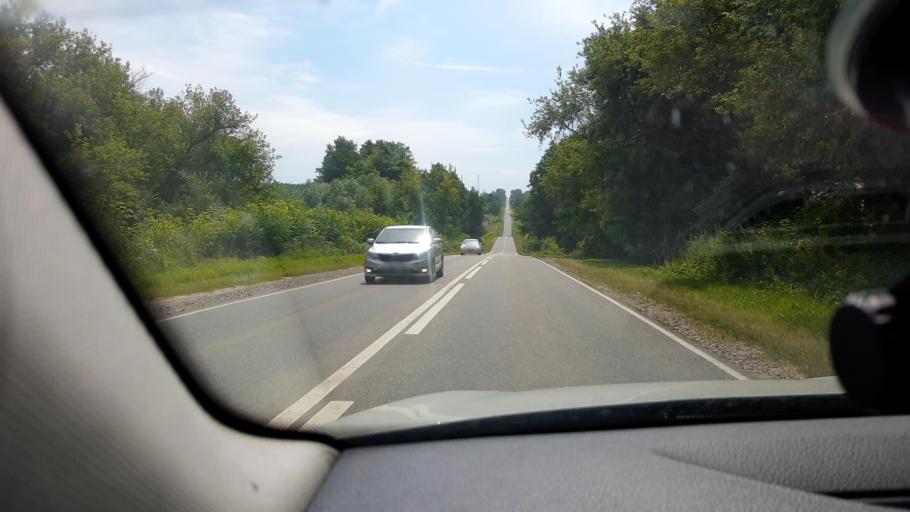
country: RU
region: Tula
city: Zaokskiy
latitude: 54.7843
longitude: 37.4341
